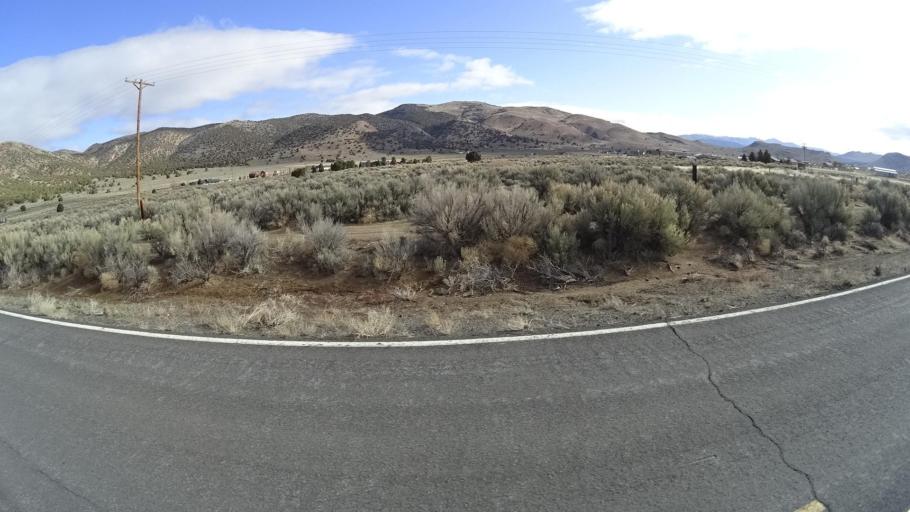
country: US
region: Nevada
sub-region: Washoe County
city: Cold Springs
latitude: 39.8980
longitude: -119.9837
